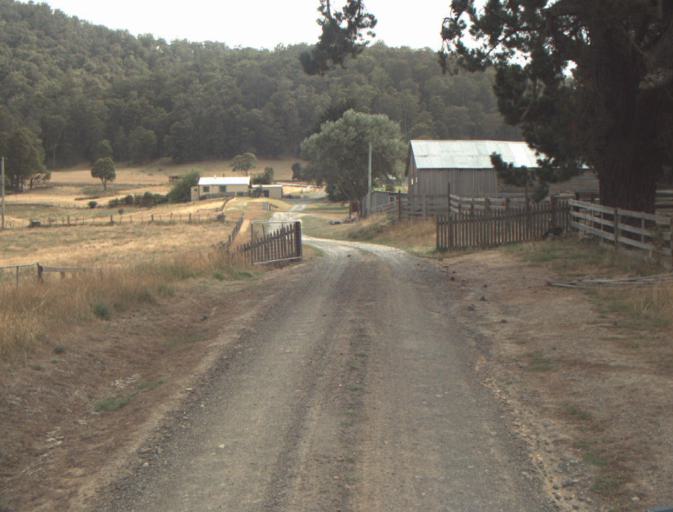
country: AU
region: Tasmania
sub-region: Dorset
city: Scottsdale
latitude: -41.4597
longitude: 147.5736
